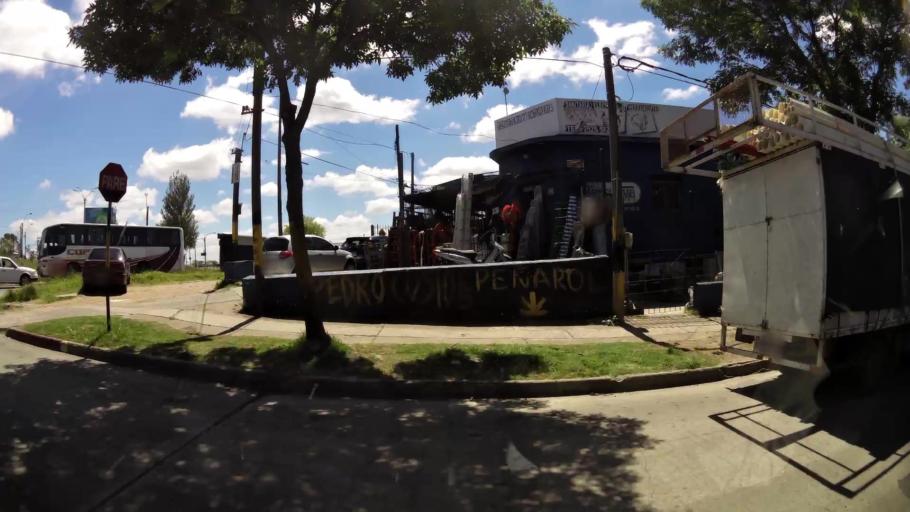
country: UY
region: Canelones
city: Paso de Carrasco
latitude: -34.8703
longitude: -56.1092
